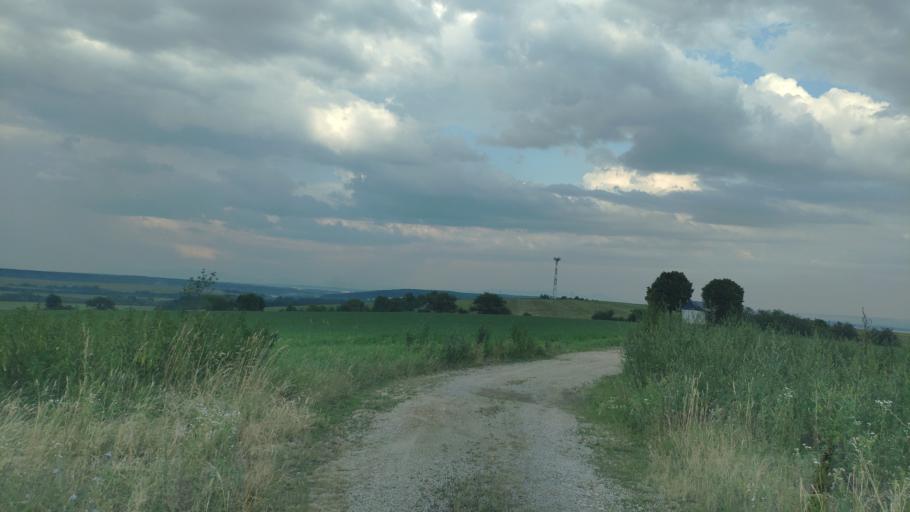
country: SK
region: Kosicky
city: Moldava nad Bodvou
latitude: 48.6870
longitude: 20.9899
